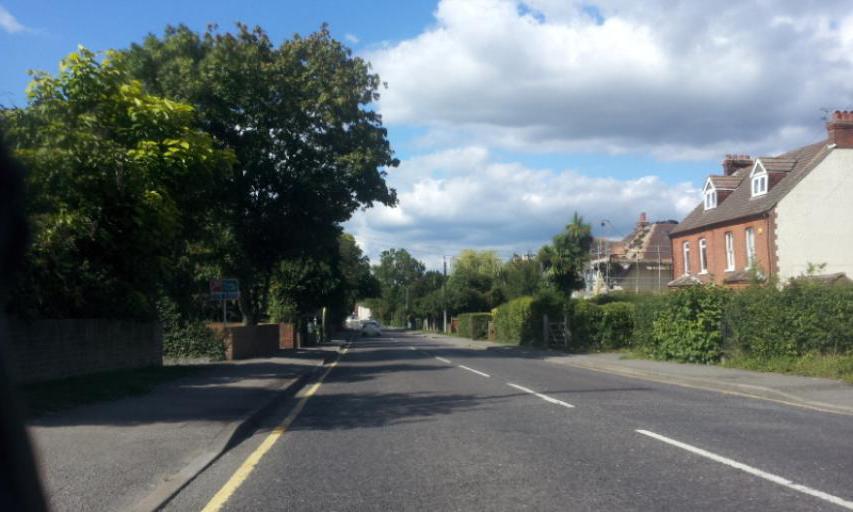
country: GB
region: England
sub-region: Kent
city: Staplehurst
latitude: 51.1672
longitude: 0.5525
